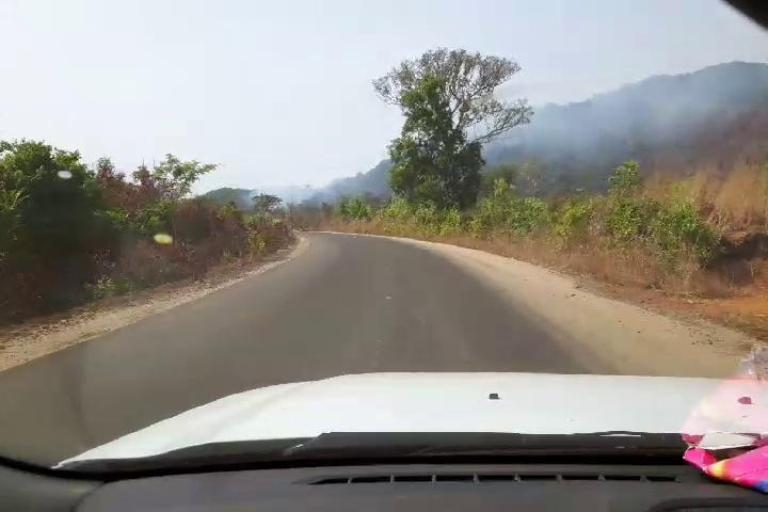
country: SL
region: Western Area
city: Waterloo
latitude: 8.2522
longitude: -13.1548
